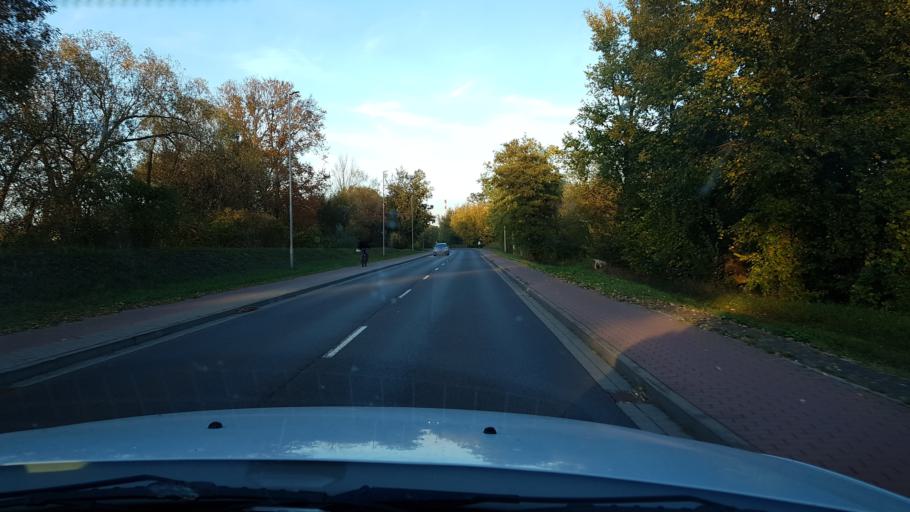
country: DE
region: Brandenburg
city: Schwedt (Oder)
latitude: 53.0745
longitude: 14.3064
